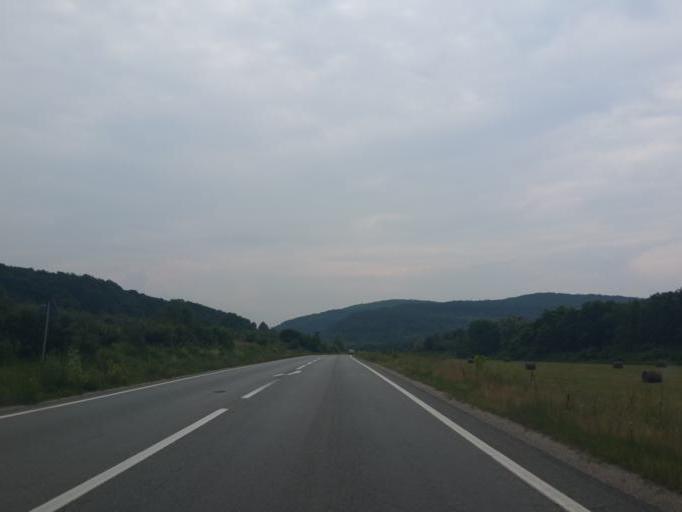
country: RO
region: Salaj
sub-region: Comuna Zimbor
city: Zimbor
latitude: 46.9639
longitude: 23.2944
